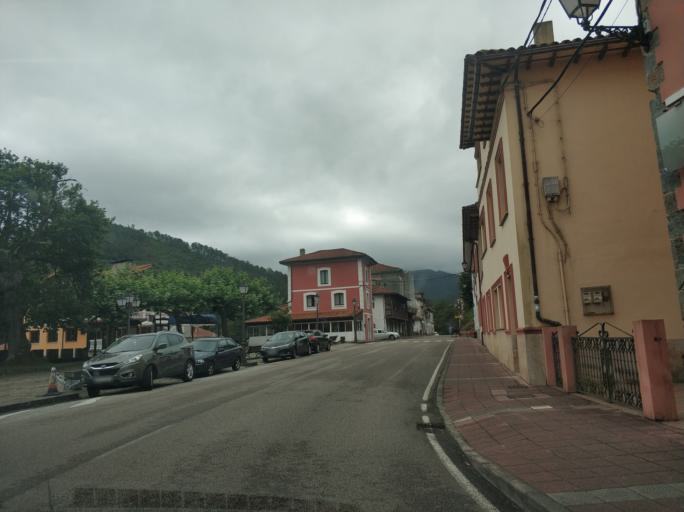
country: ES
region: Asturias
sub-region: Province of Asturias
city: Cudillero
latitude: 43.5618
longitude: -6.2309
